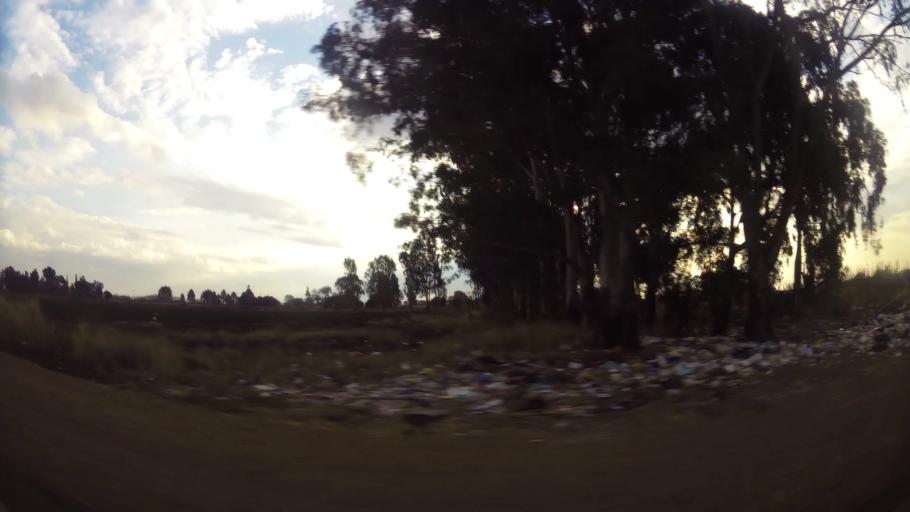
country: ZA
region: Gauteng
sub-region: Sedibeng District Municipality
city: Vanderbijlpark
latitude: -26.6417
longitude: 27.8053
